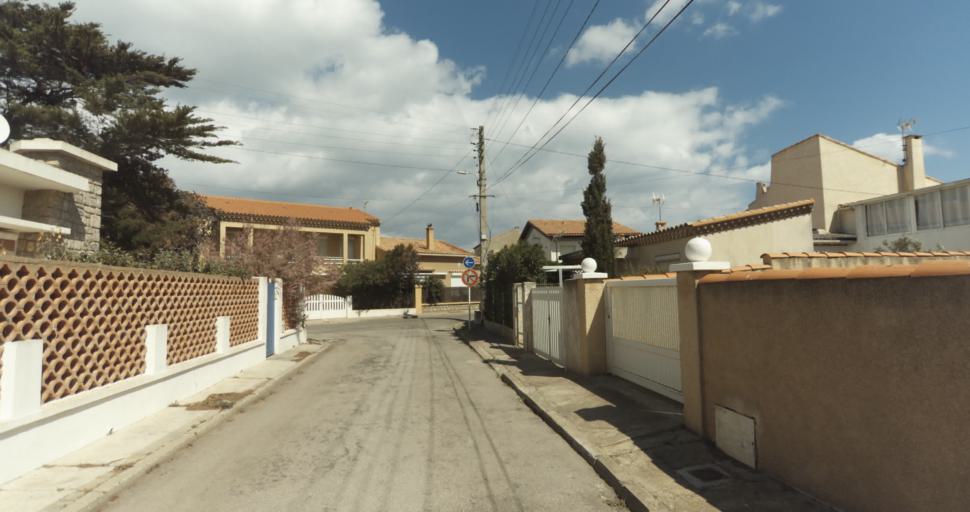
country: FR
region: Languedoc-Roussillon
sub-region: Departement de l'Aude
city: Leucate
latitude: 42.9040
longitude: 3.0549
